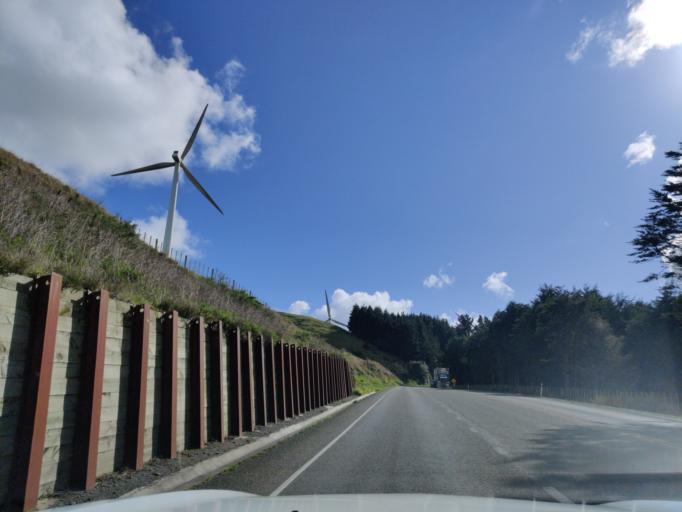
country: NZ
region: Manawatu-Wanganui
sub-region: Palmerston North City
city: Palmerston North
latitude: -40.2984
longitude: 175.8104
